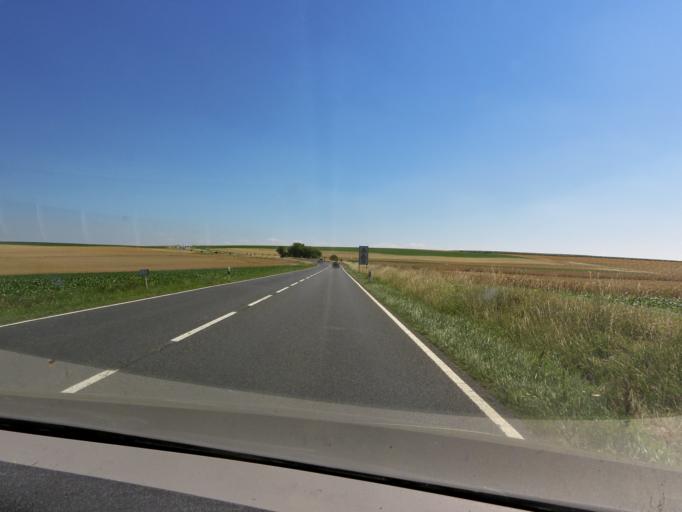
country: DE
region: Bavaria
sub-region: Regierungsbezirk Unterfranken
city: Reichenberg
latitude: 49.7269
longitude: 9.9333
